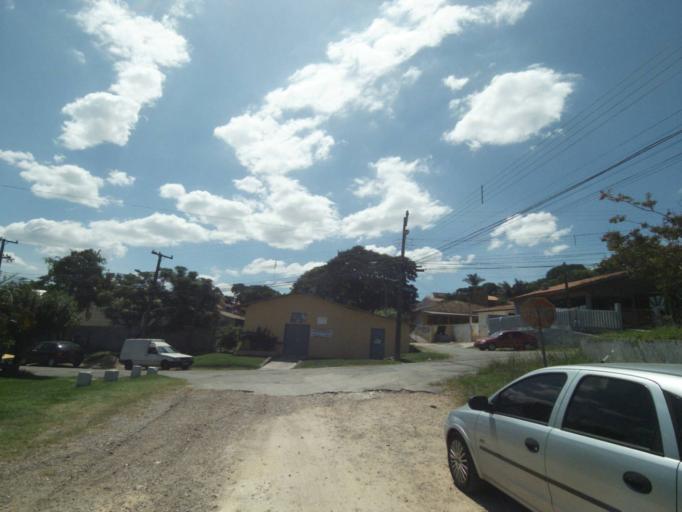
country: BR
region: Parana
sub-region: Curitiba
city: Curitiba
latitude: -25.4680
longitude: -49.2467
